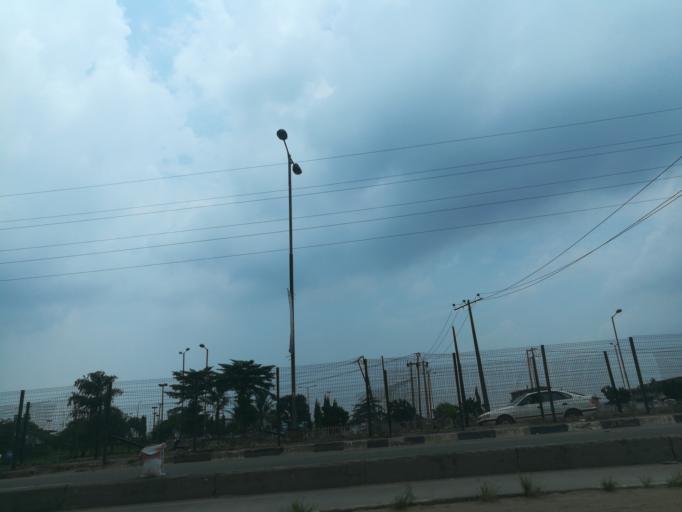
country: NG
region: Lagos
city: Ojota
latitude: 6.5924
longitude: 3.3820
